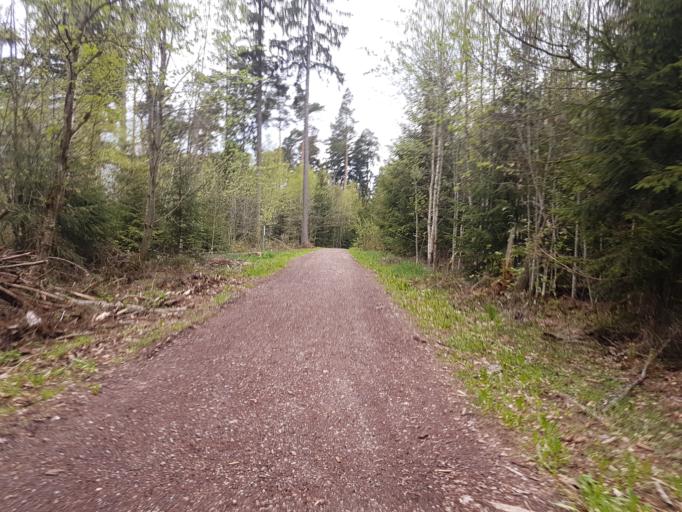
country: DE
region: Baden-Wuerttemberg
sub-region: Freiburg Region
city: Bad Durrheim
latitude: 48.0428
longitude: 8.5220
